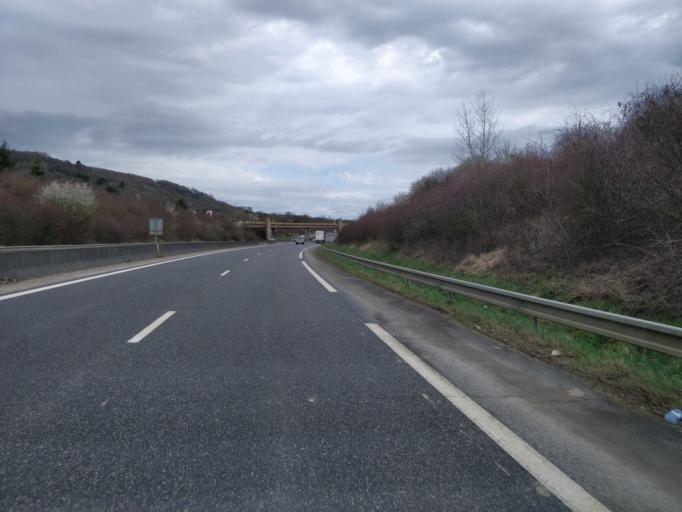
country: FR
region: Lorraine
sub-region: Departement de la Moselle
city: Vitry-sur-Orne
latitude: 49.2688
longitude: 6.1099
